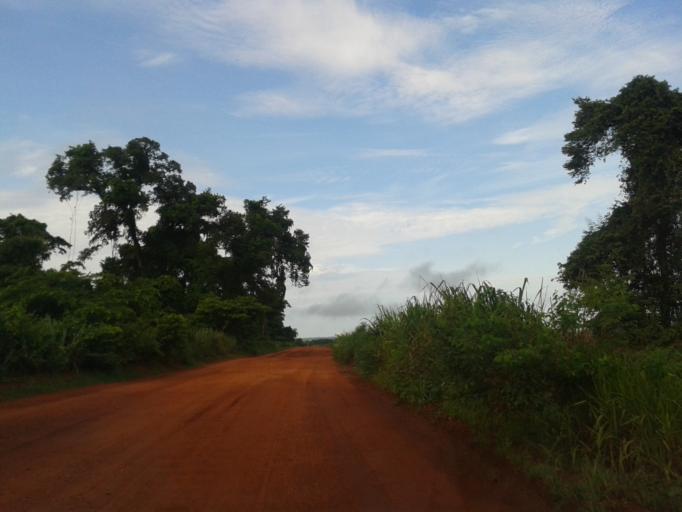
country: BR
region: Minas Gerais
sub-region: Santa Vitoria
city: Santa Vitoria
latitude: -19.1256
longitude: -50.5437
